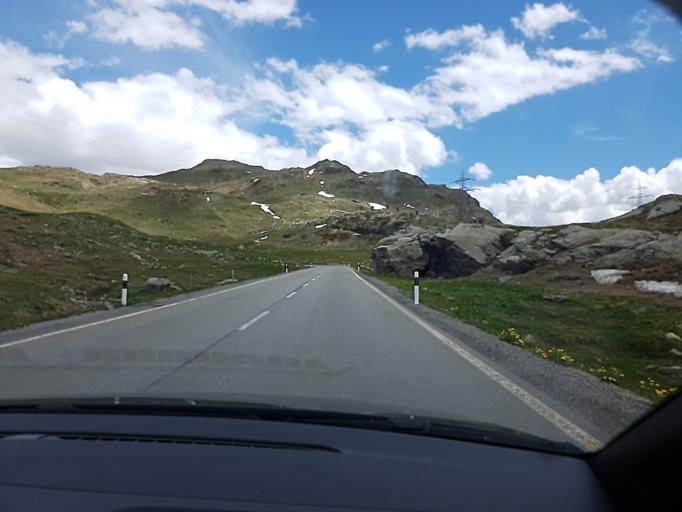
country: CH
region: Grisons
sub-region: Bernina District
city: Poschiavo
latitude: 46.4156
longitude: 10.0152
